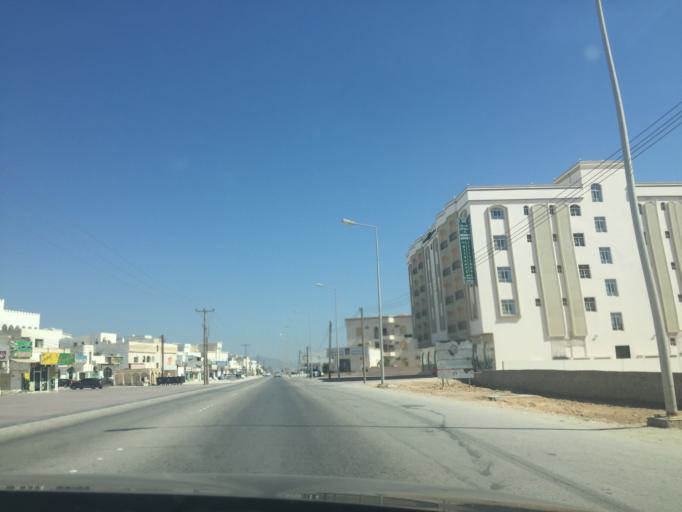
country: OM
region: Zufar
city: Salalah
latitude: 17.0201
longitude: 54.1613
